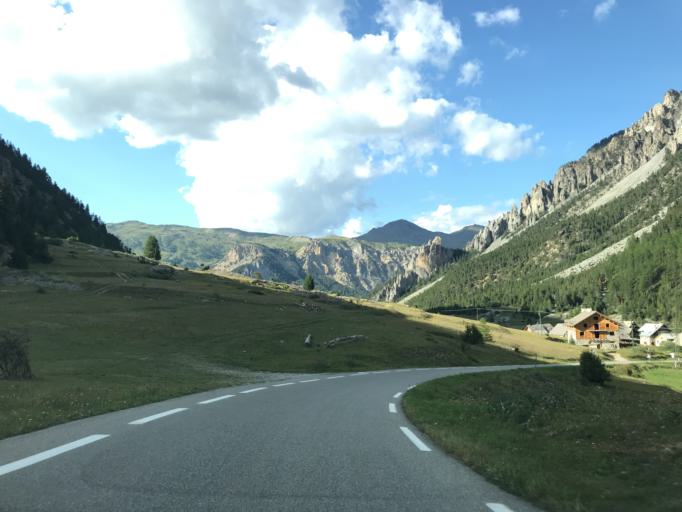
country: IT
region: Piedmont
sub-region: Provincia di Torino
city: Claviere
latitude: 44.8525
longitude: 6.7245
